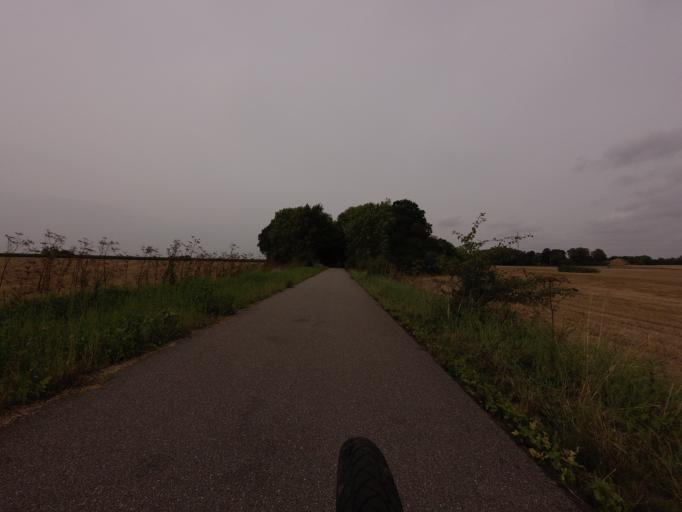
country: DK
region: Zealand
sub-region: Naestved Kommune
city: Fuglebjerg
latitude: 55.2679
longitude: 11.4847
